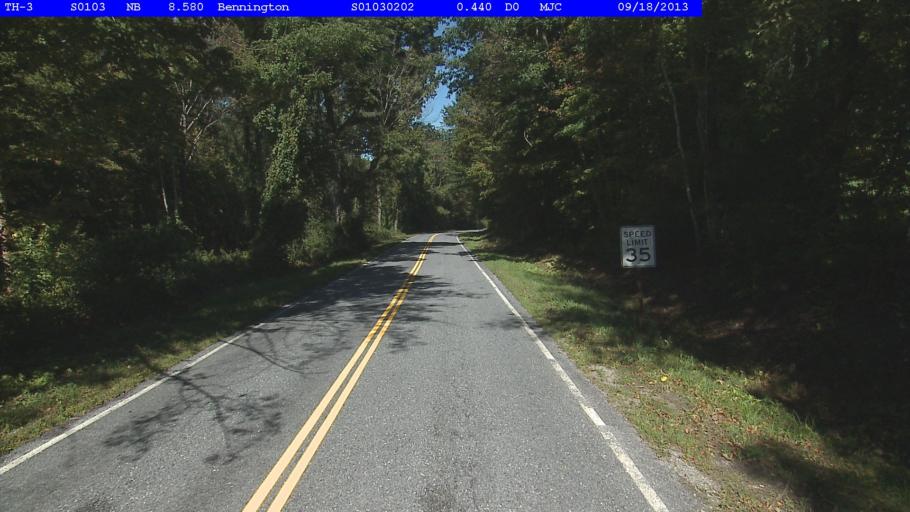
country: US
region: Vermont
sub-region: Bennington County
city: Bennington
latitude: 42.8431
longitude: -73.1725
